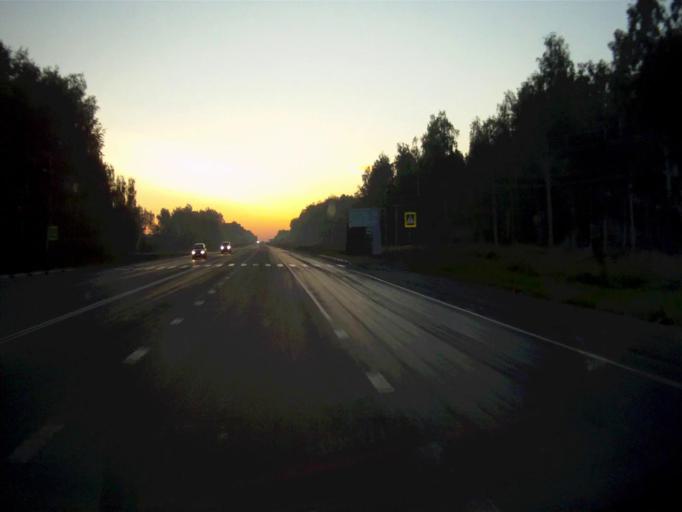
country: RU
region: Chelyabinsk
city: Poletayevo
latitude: 55.2067
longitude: 61.1040
